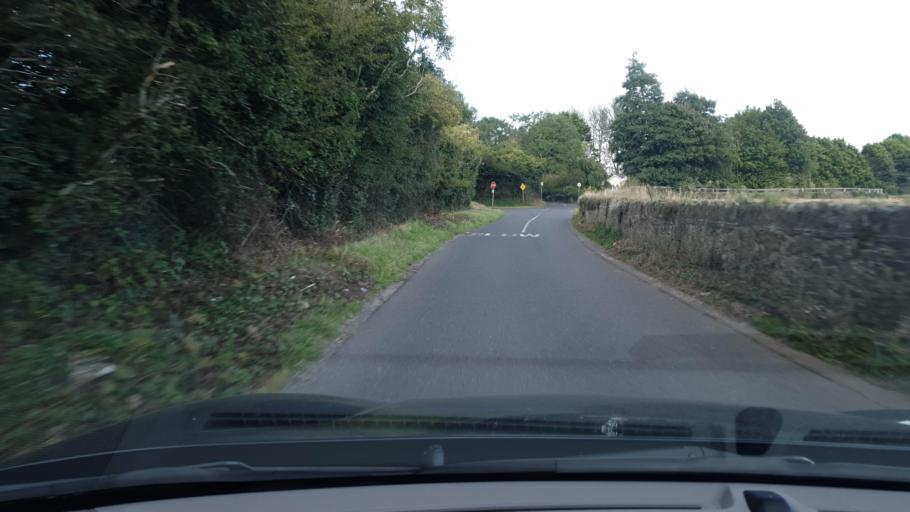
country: IE
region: Leinster
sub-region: South Dublin
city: Newcastle
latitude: 53.2659
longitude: -6.5151
